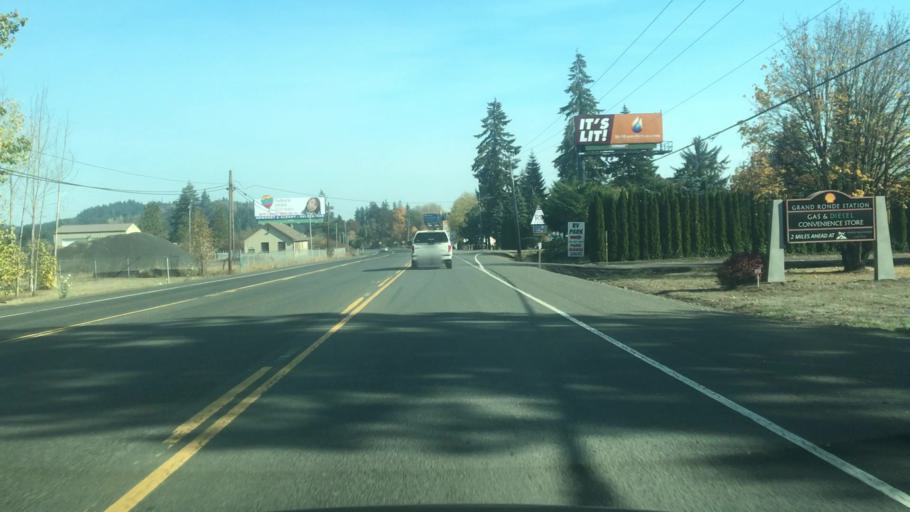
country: US
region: Oregon
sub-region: Polk County
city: Grand Ronde
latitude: 45.0583
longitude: -123.6191
